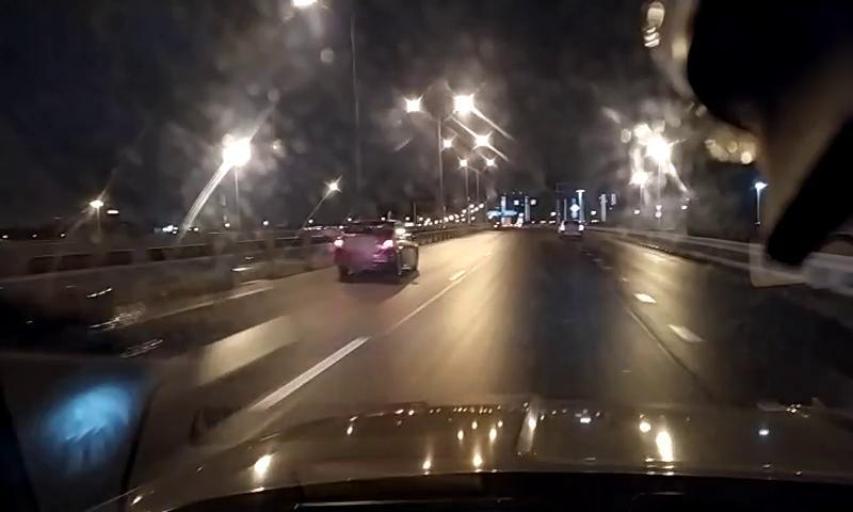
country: RU
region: Leningrad
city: Bugry
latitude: 60.0932
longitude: 30.3711
